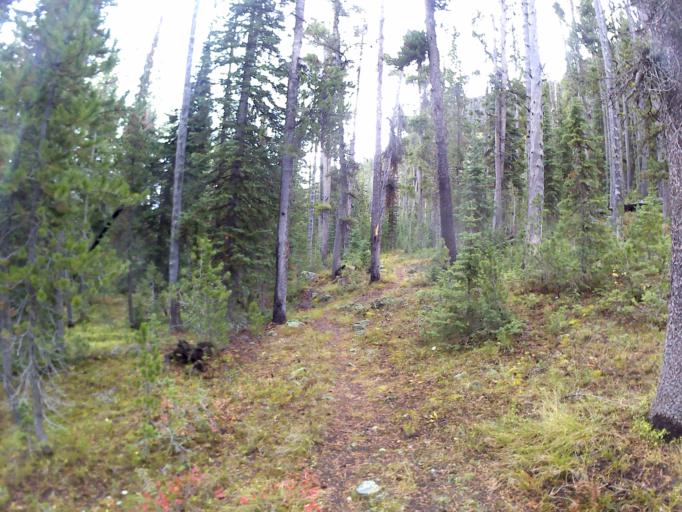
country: US
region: Montana
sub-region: Gallatin County
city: West Yellowstone
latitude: 44.4293
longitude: -110.7471
